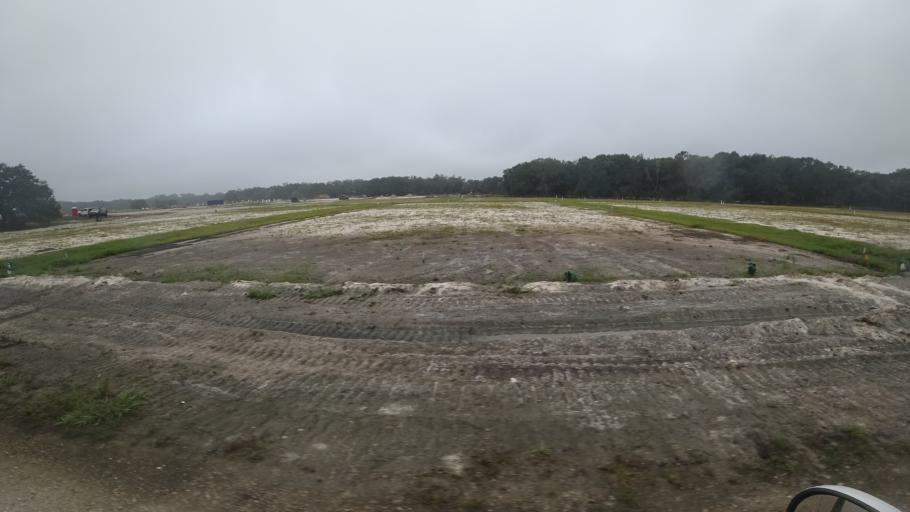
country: US
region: Florida
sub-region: Sarasota County
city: Lake Sarasota
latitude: 27.2935
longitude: -82.2209
